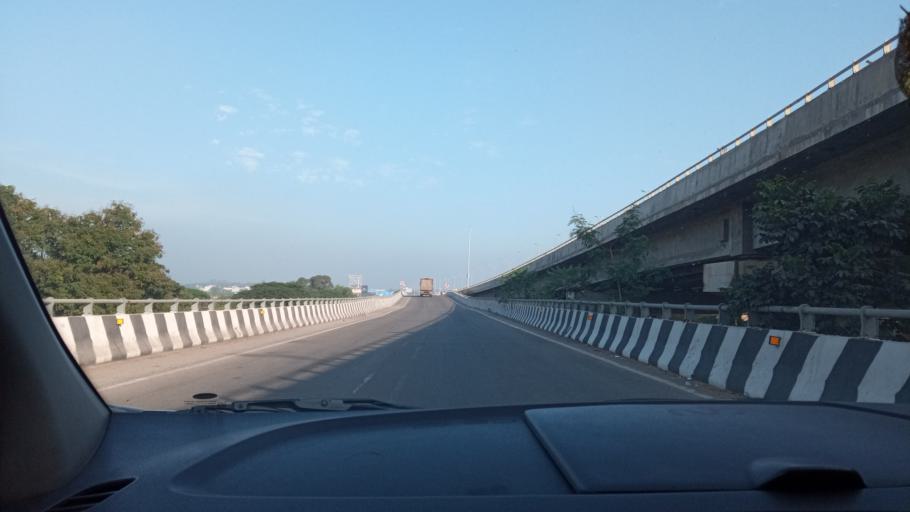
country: IN
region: Telangana
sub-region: Hyderabad
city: Hyderabad
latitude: 17.3240
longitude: 78.3748
